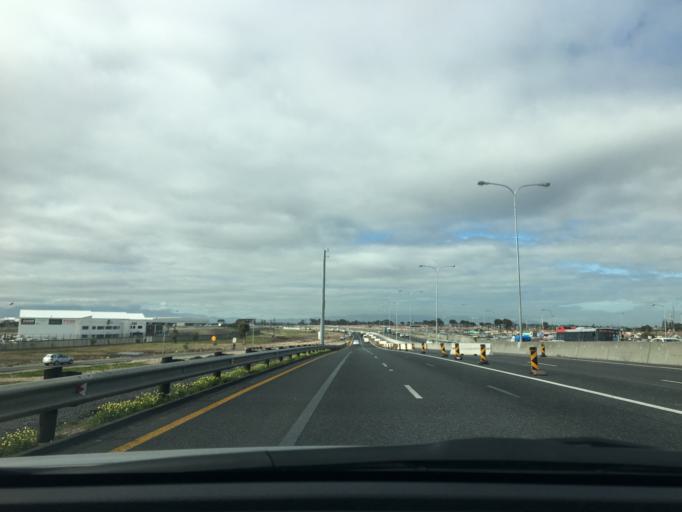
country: ZA
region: Western Cape
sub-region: City of Cape Town
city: Lansdowne
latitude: -33.9824
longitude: 18.5883
